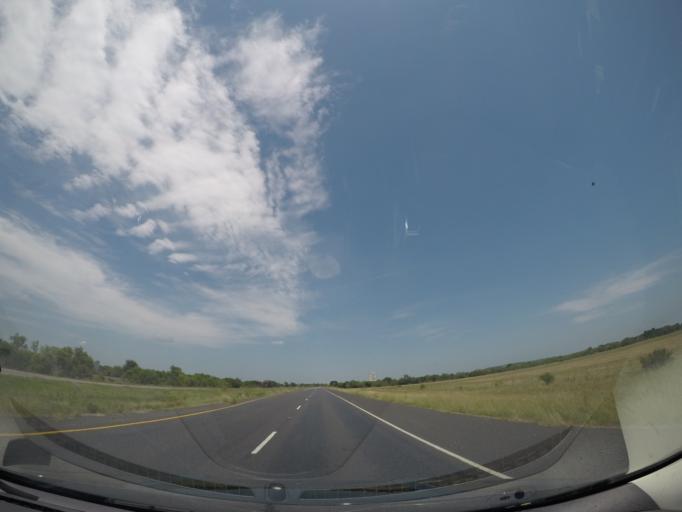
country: US
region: Texas
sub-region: Medina County
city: Hondo
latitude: 29.3254
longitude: -99.2984
